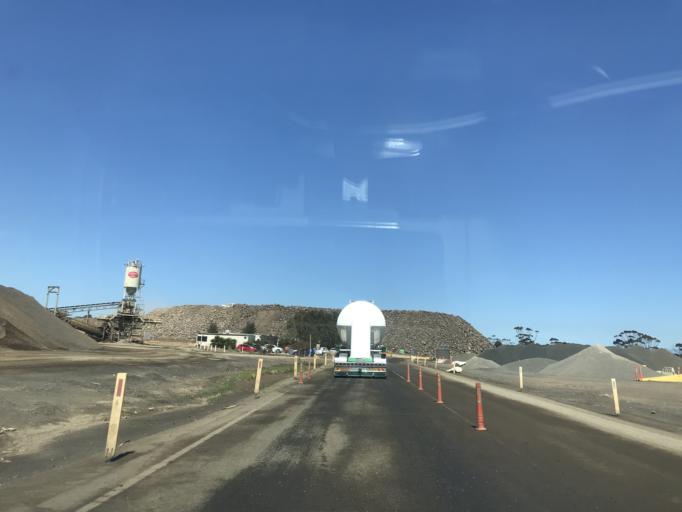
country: AU
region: Victoria
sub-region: Wyndham
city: Truganina
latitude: -37.8324
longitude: 144.7720
